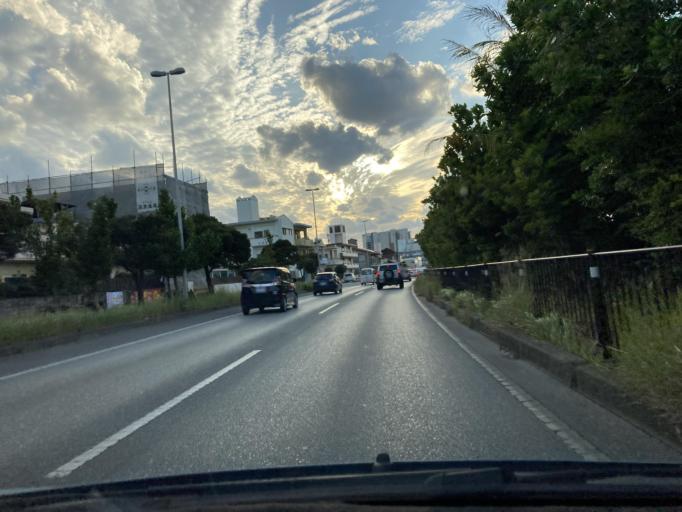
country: JP
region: Okinawa
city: Ginowan
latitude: 26.2801
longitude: 127.7402
